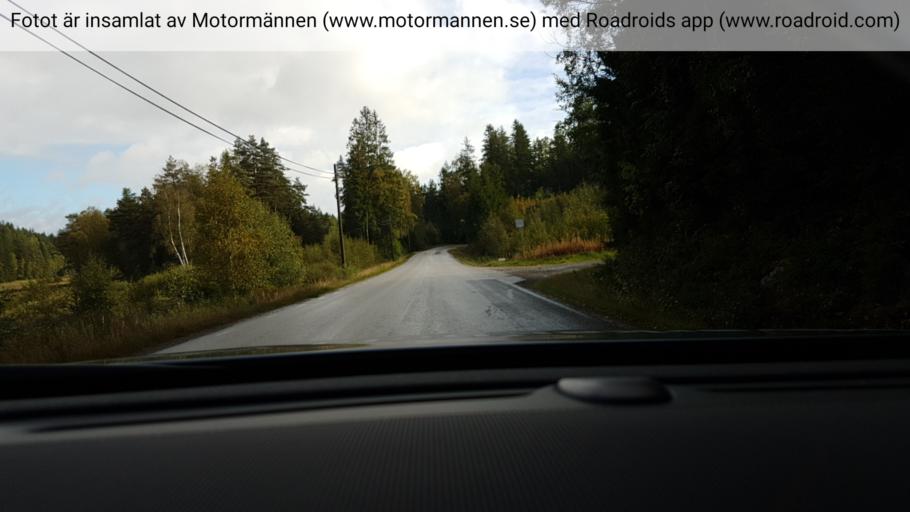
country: SE
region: Vaestra Goetaland
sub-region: Marks Kommun
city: Fritsla
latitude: 57.4027
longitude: 12.8412
